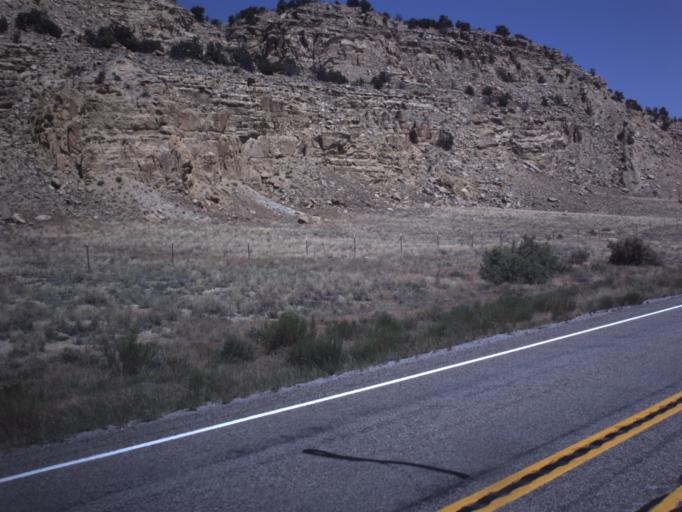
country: US
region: Utah
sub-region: Emery County
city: Ferron
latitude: 38.8277
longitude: -111.3235
